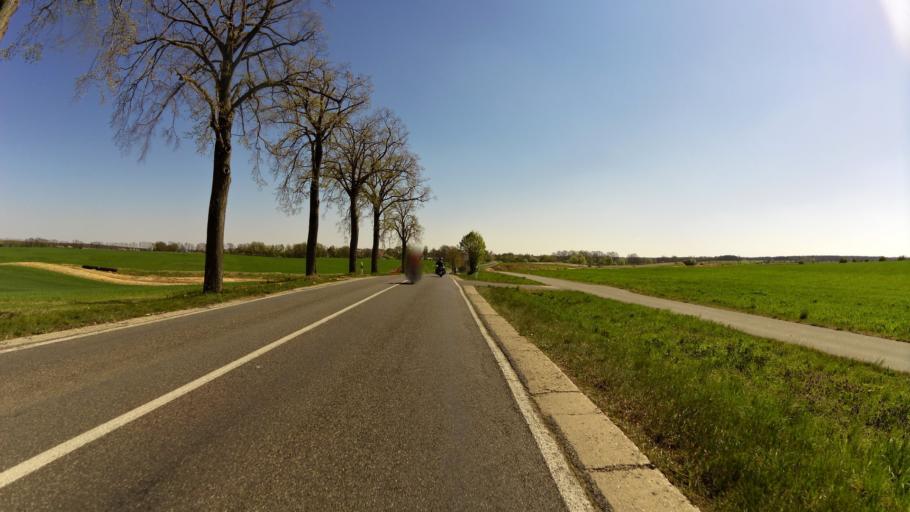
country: DE
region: Brandenburg
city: Strausberg
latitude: 52.5686
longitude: 13.9571
